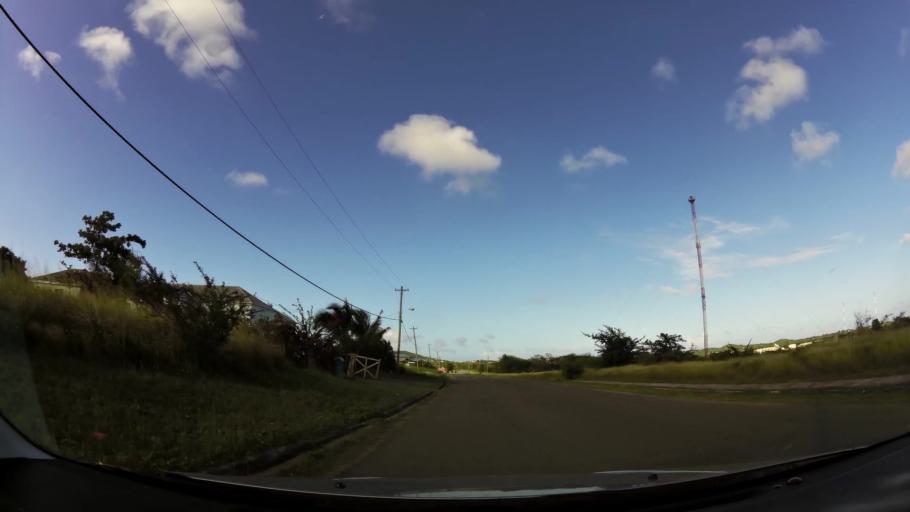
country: AG
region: Saint George
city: Piggotts
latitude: 17.0987
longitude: -61.8014
